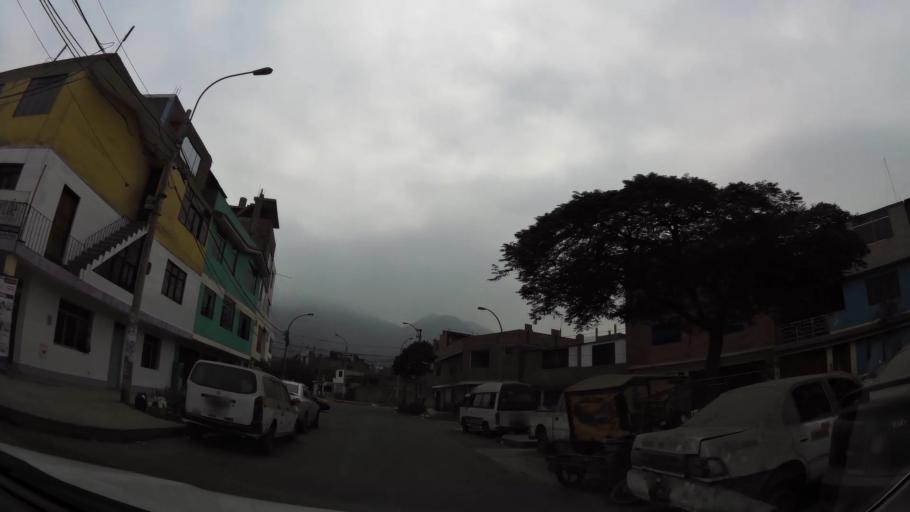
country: PE
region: Lima
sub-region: Lima
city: Independencia
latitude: -11.9942
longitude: -77.0072
